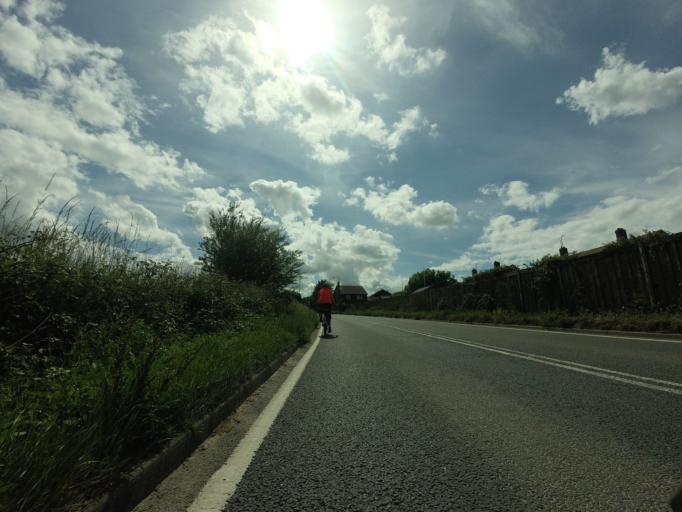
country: GB
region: England
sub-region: Medway
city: Stoke
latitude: 51.4515
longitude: 0.6360
